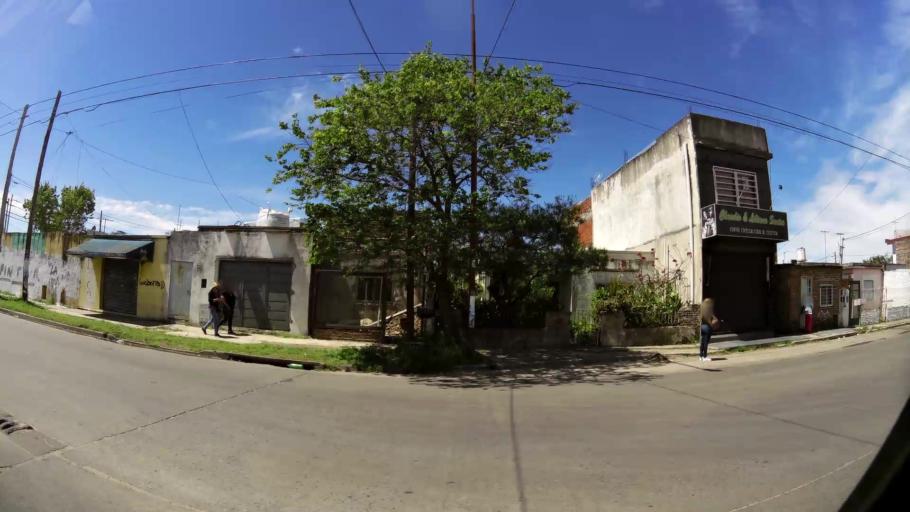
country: AR
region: Buenos Aires
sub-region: Partido de Quilmes
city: Quilmes
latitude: -34.7353
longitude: -58.3005
